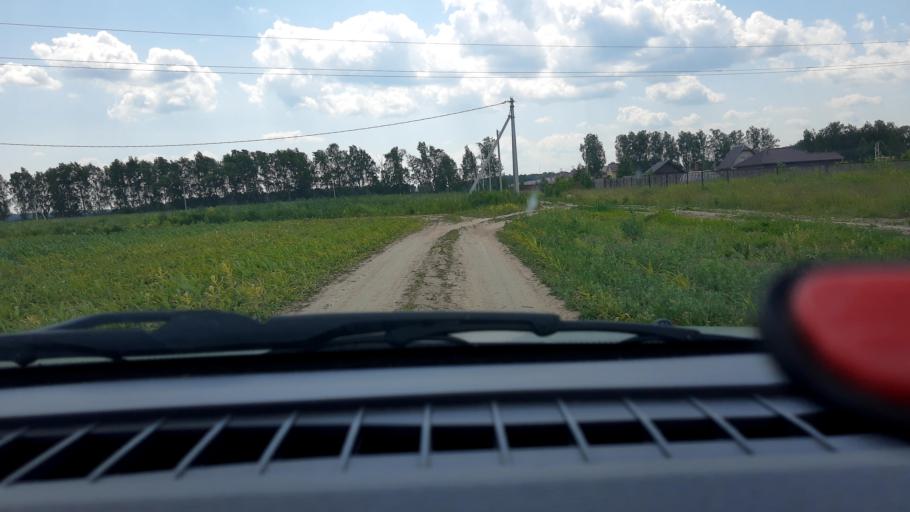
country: RU
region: Nizjnij Novgorod
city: Afonino
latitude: 56.1219
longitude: 44.0296
